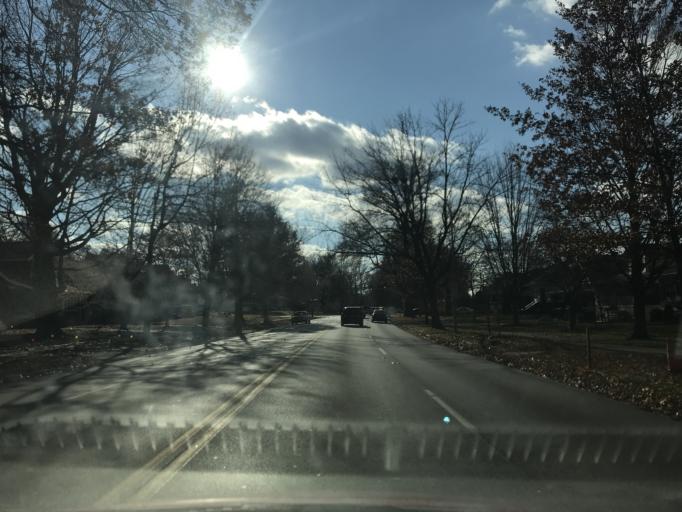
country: US
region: Kentucky
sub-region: Jefferson County
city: Audubon Park
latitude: 38.2196
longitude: -85.7344
